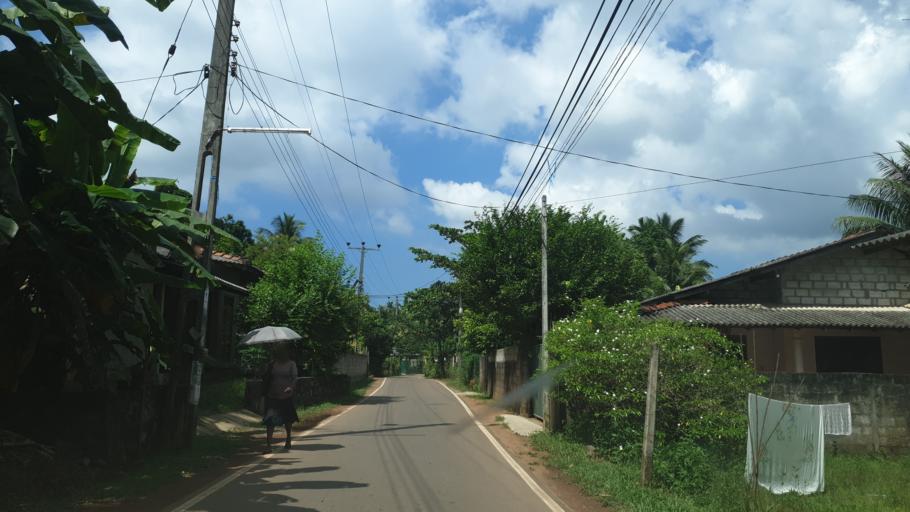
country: LK
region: Western
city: Panadura
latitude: 6.6758
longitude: 79.9722
